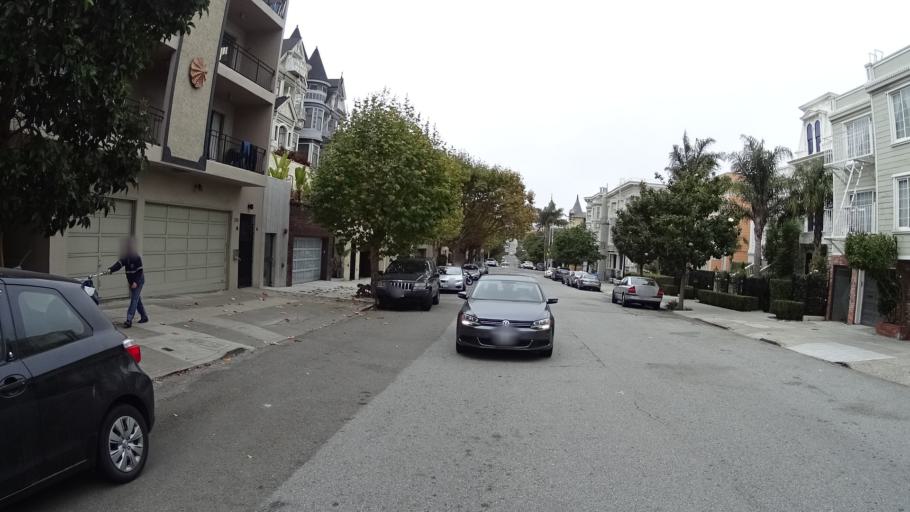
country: US
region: California
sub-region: San Francisco County
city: San Francisco
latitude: 37.7963
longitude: -122.4343
